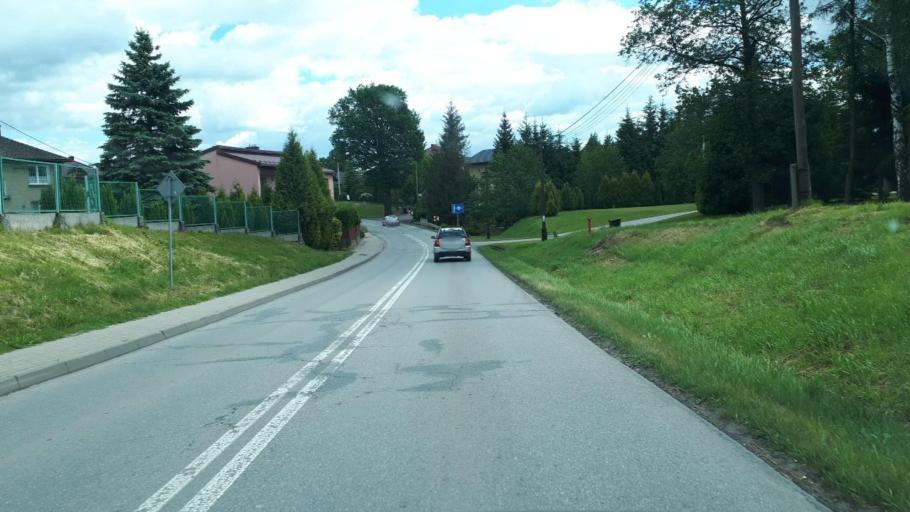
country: PL
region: Lesser Poland Voivodeship
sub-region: Powiat oswiecimski
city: Brzeszcze
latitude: 49.9582
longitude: 19.1378
